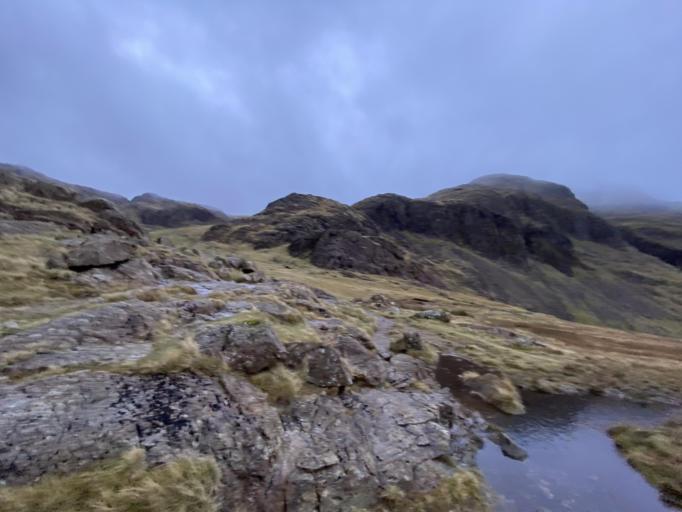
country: GB
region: England
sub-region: Cumbria
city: Keswick
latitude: 54.4746
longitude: -3.2028
